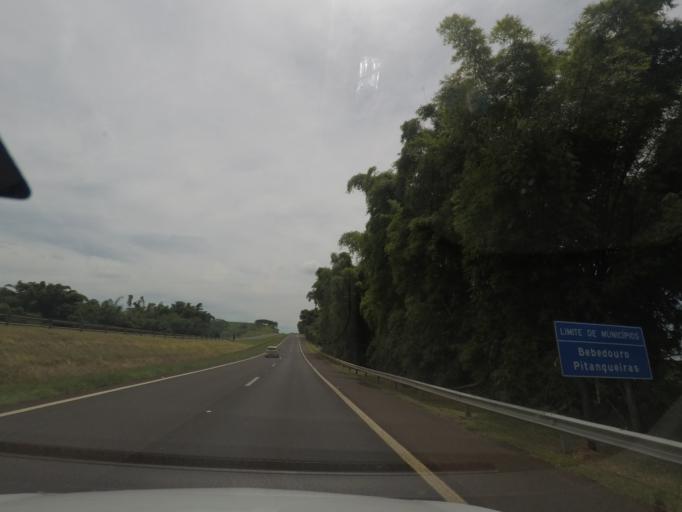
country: BR
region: Sao Paulo
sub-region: Bebedouro
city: Bebedouro
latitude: -21.0290
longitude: -48.4212
